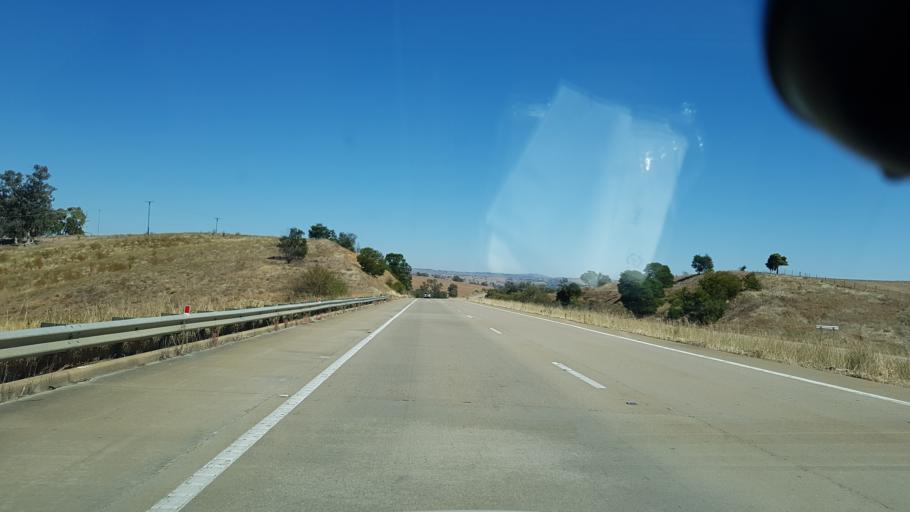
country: AU
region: New South Wales
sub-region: Gundagai
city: Gundagai
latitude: -34.8134
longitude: 148.4139
